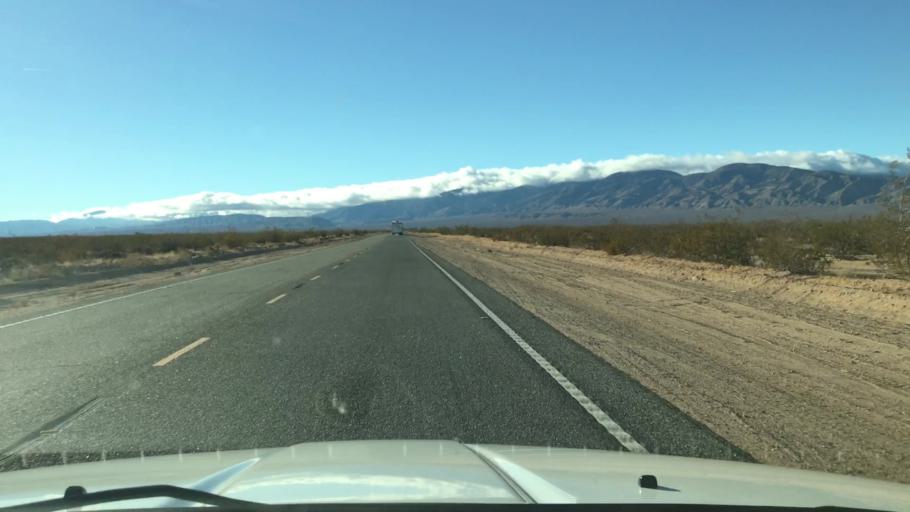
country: US
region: California
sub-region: Kern County
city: California City
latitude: 35.1255
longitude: -118.0605
